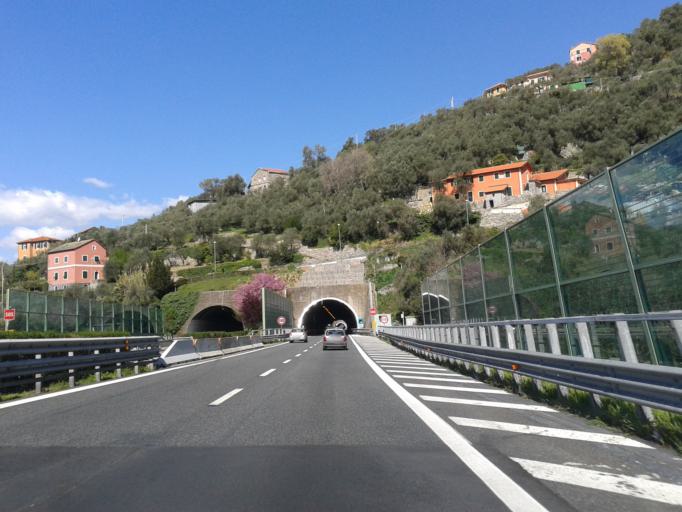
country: IT
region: Liguria
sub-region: Provincia di Genova
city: Rapallo
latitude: 44.3498
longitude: 9.2480
